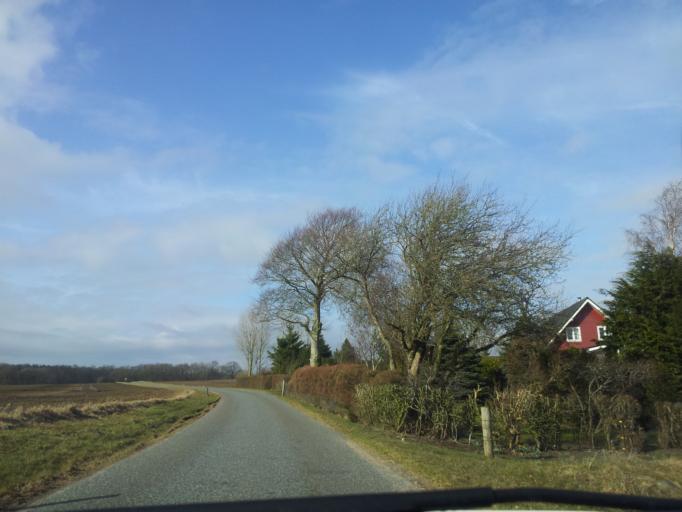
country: DK
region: South Denmark
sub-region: Vejen Kommune
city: Brorup
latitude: 55.4481
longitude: 9.0459
